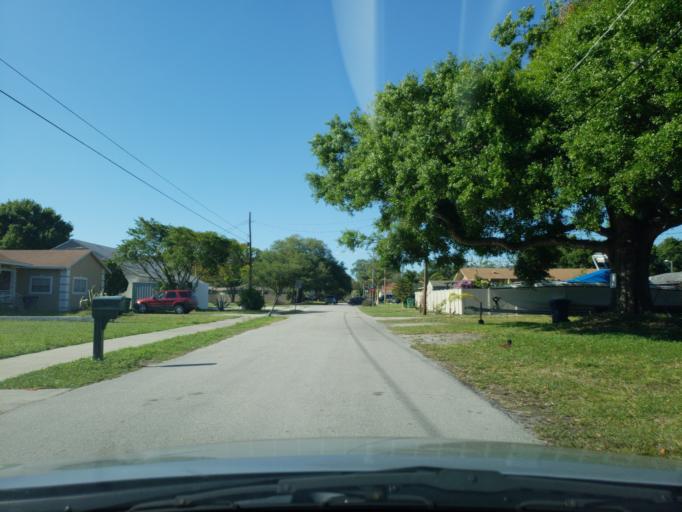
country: US
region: Florida
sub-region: Hillsborough County
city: Tampa
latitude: 27.9513
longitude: -82.4953
